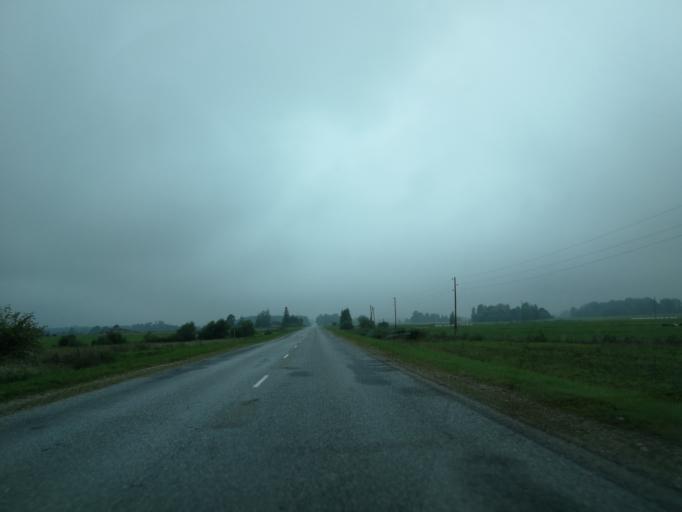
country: LV
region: Varkava
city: Vecvarkava
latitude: 56.3085
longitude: 26.5803
